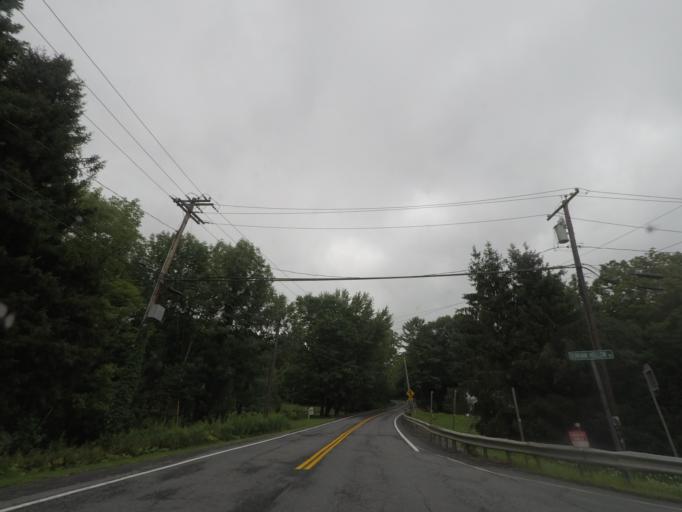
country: US
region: New York
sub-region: Rensselaer County
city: Averill Park
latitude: 42.5852
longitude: -73.4849
